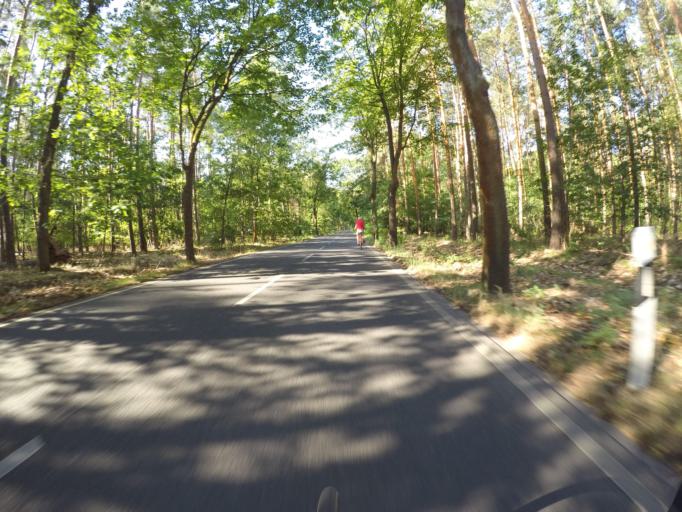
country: DE
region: Berlin
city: Schmockwitz
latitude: 52.3613
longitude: 13.6525
